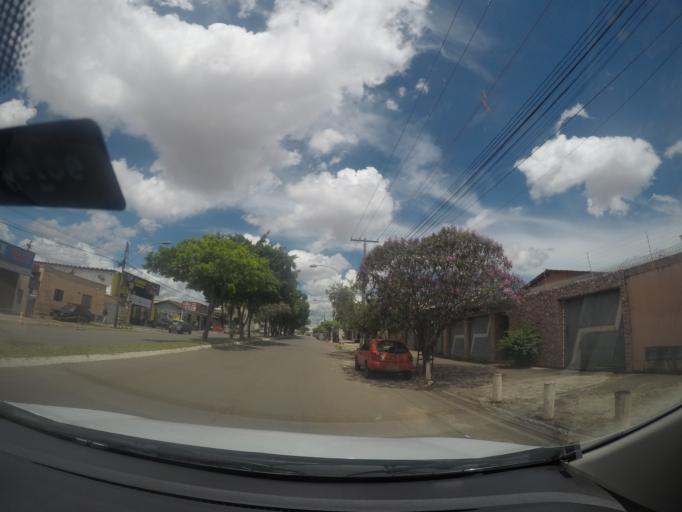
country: BR
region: Goias
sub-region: Goiania
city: Goiania
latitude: -16.6765
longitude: -49.3144
